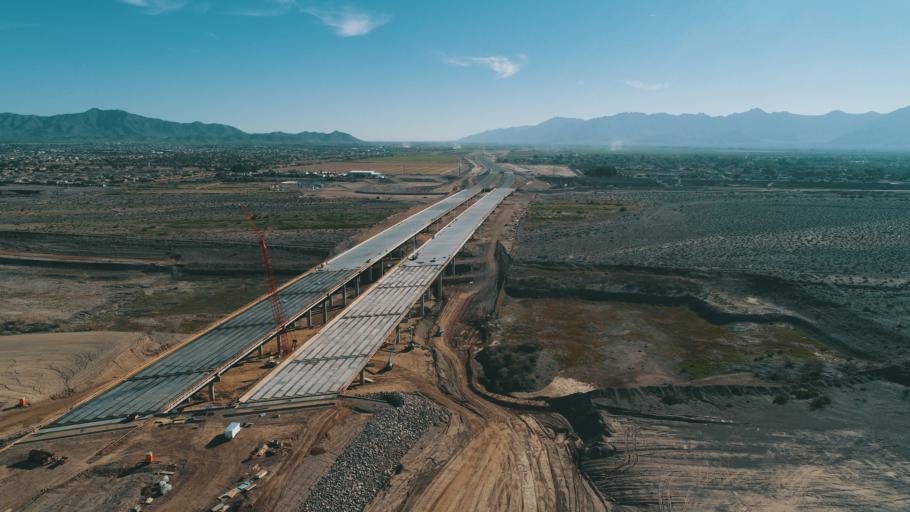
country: US
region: Arizona
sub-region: Maricopa County
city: Laveen
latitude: 33.4043
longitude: -112.1931
